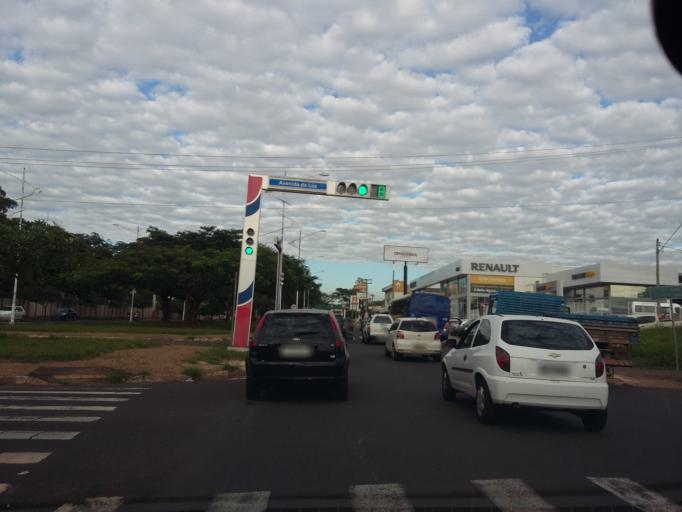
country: BR
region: Sao Paulo
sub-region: Sao Jose Do Rio Preto
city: Sao Jose do Rio Preto
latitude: -20.8226
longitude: -49.4007
